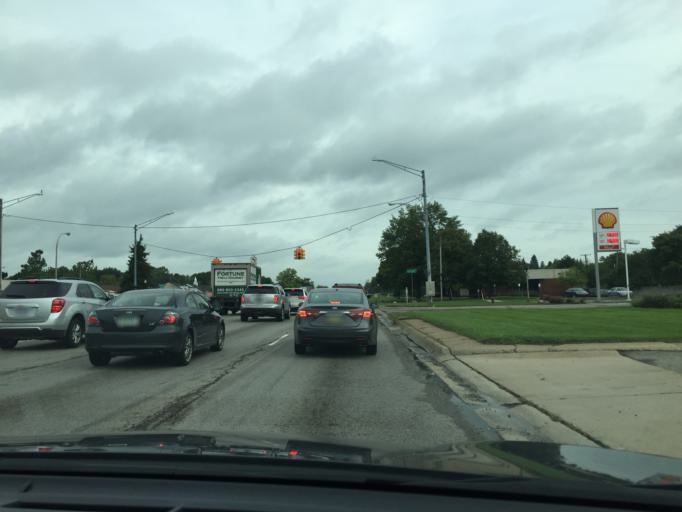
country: US
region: Michigan
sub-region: Oakland County
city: Southfield
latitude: 42.4799
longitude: -83.2213
